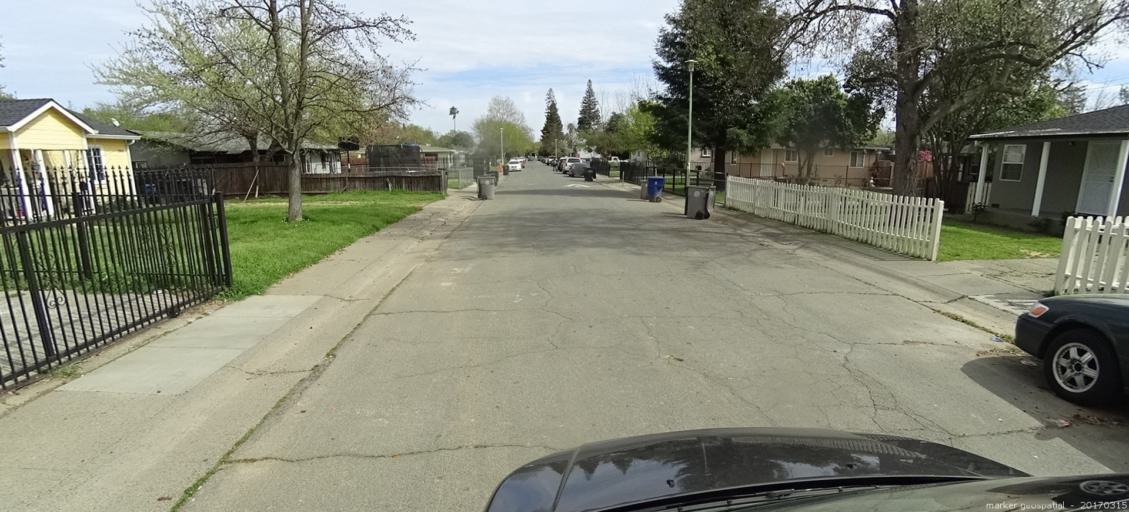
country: US
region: California
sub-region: Sacramento County
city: Parkway
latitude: 38.5224
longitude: -121.4754
